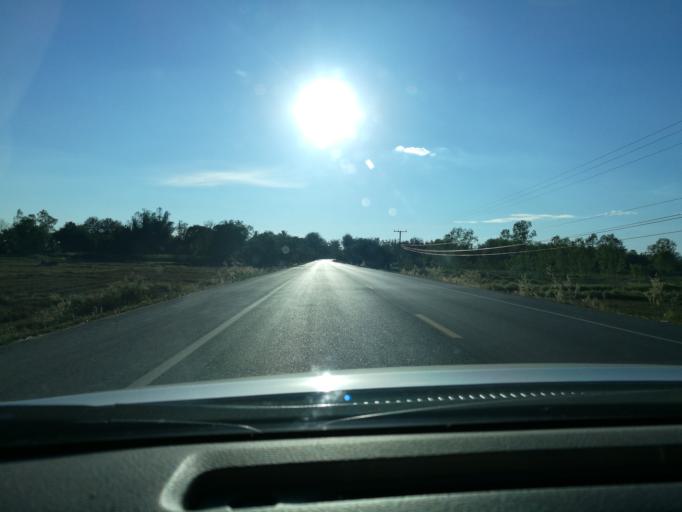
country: TH
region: Phitsanulok
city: Nakhon Thai
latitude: 17.0703
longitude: 100.8215
